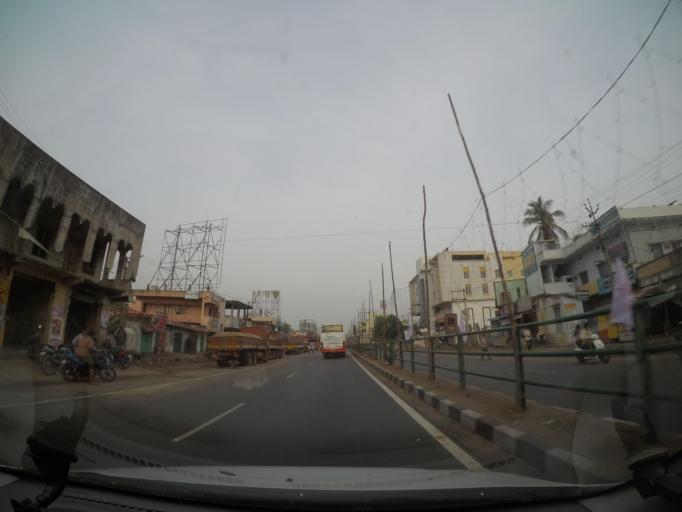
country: IN
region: Andhra Pradesh
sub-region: West Godavari
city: Eluru
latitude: 16.6359
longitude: 80.9733
